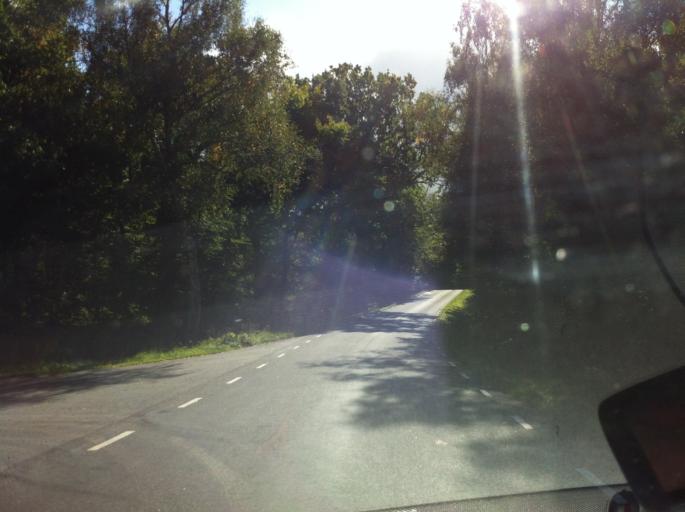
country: SE
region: Skane
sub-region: Kristianstads Kommun
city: Degeberga
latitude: 55.7533
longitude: 13.9394
